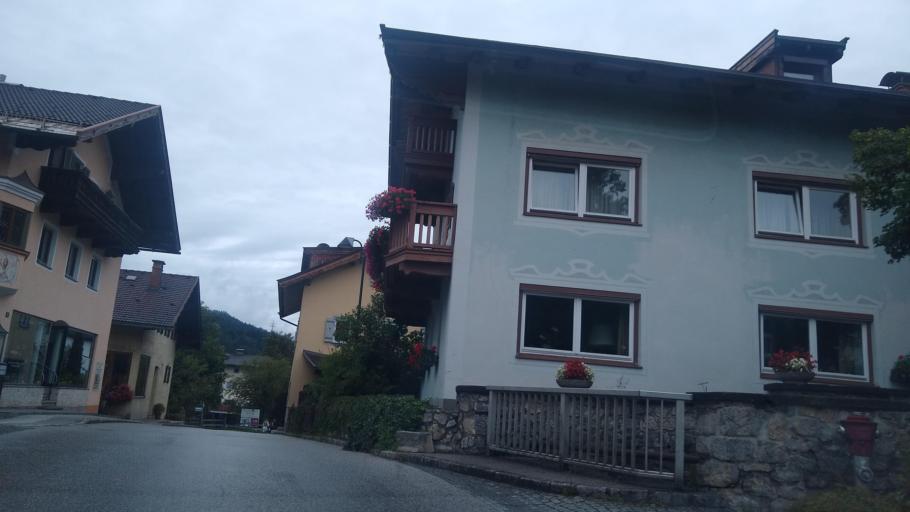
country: AT
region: Tyrol
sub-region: Politischer Bezirk Kitzbuhel
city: Hopfgarten im Brixental
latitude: 47.4490
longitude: 12.1574
